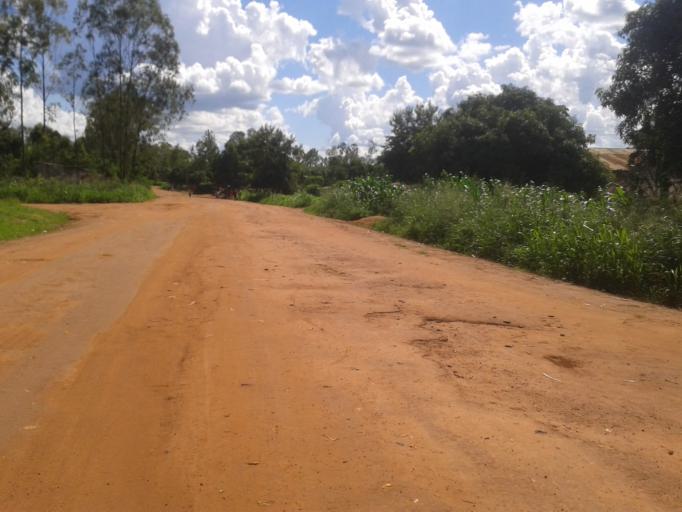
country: UG
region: Northern Region
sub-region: Gulu District
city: Gulu
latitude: 2.7582
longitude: 32.3115
